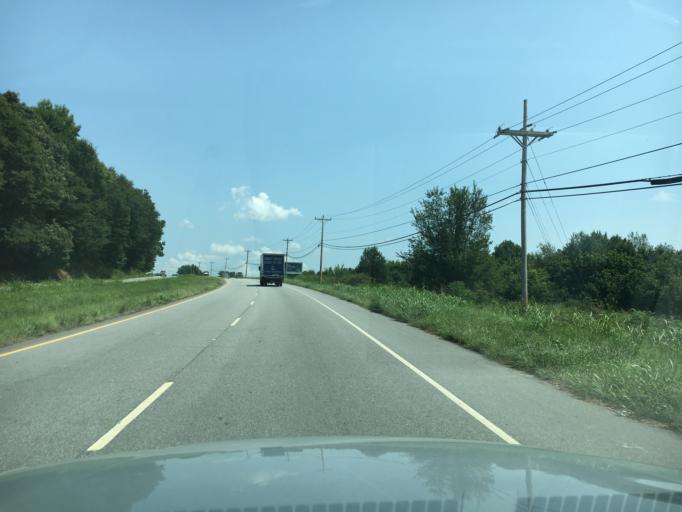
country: US
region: South Carolina
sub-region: Anderson County
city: Northlake
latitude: 34.5827
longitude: -82.7352
